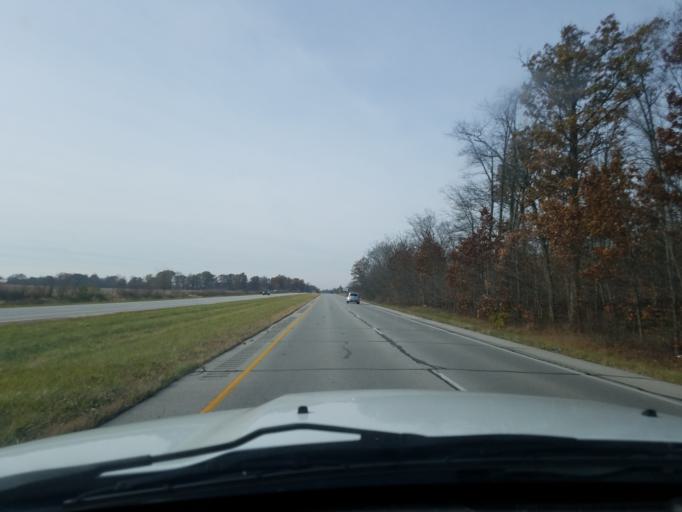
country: US
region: Indiana
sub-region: Delaware County
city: Yorktown
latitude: 40.2193
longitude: -85.4921
